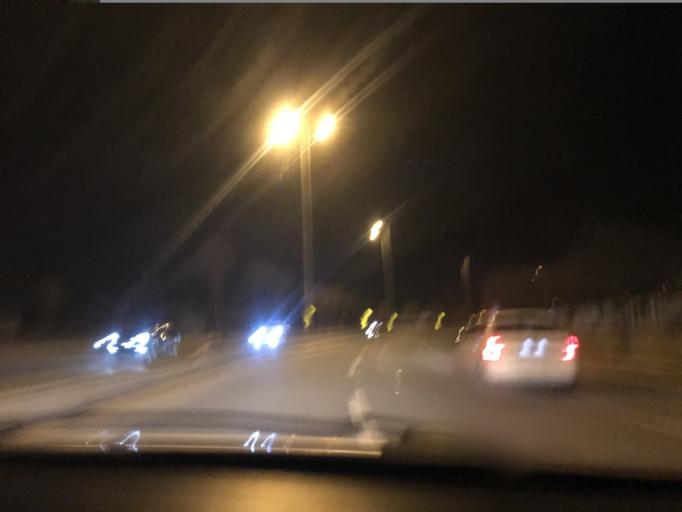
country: TR
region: Ankara
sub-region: Goelbasi
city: Golbasi
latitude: 39.8446
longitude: 32.7913
